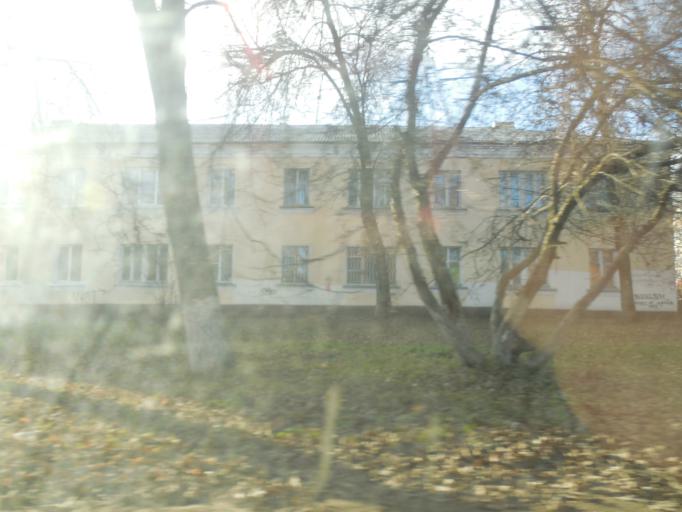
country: RU
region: Tula
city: Mendeleyevskiy
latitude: 54.1641
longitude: 37.5959
